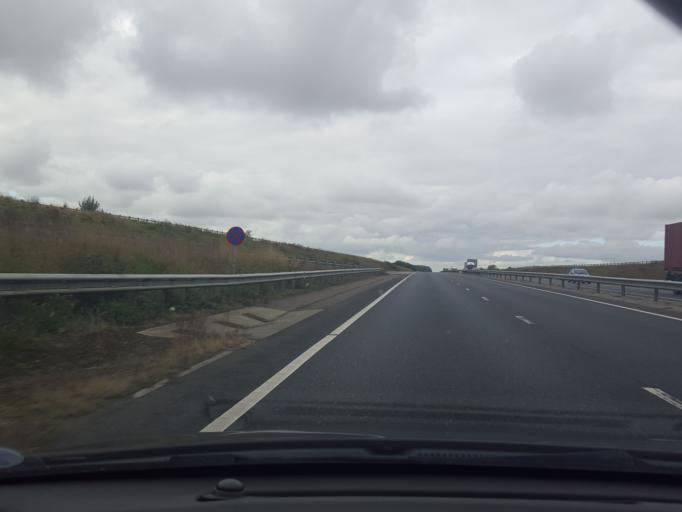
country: GB
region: England
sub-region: Suffolk
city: Stowmarket
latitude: 52.2068
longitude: 0.9726
